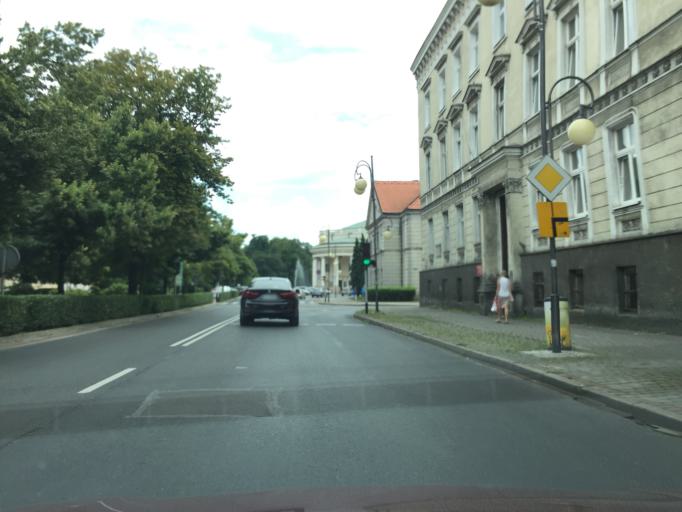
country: PL
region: Greater Poland Voivodeship
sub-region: Kalisz
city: Kalisz
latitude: 51.7595
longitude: 18.0917
